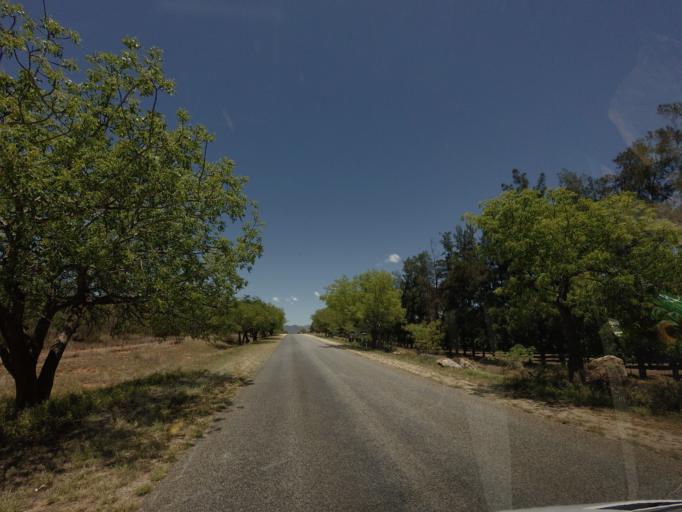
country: ZA
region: Limpopo
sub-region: Mopani District Municipality
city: Hoedspruit
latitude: -24.3741
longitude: 30.7069
